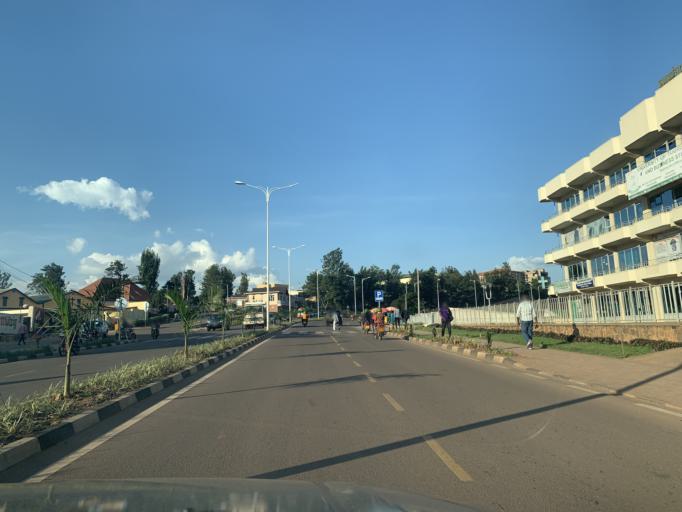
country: RW
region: Kigali
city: Kigali
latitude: -1.9665
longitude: 30.1030
